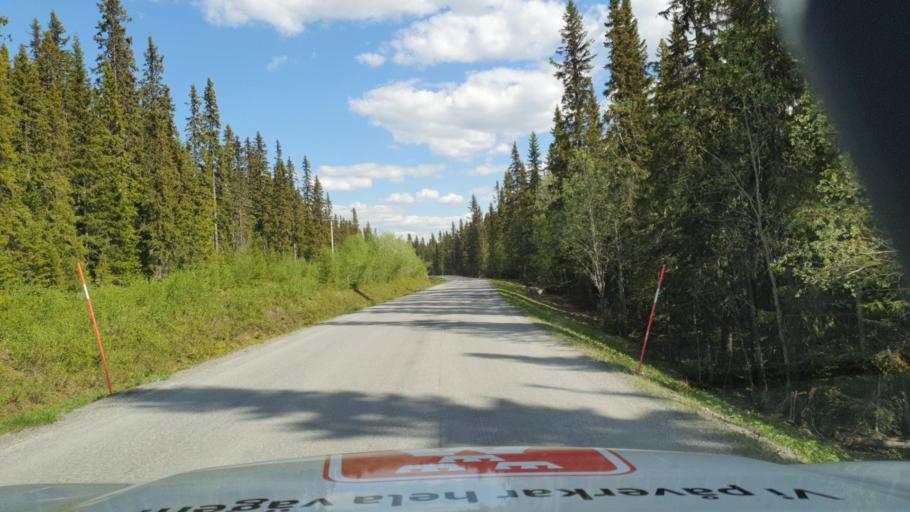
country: SE
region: Jaemtland
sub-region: Krokoms Kommun
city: Krokom
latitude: 63.6807
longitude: 14.2626
